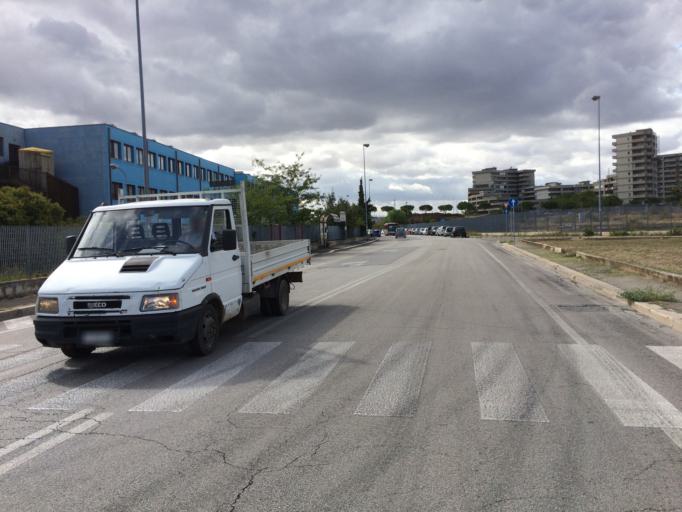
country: IT
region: Apulia
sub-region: Provincia di Bari
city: Bari
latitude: 41.0959
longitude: 16.8576
